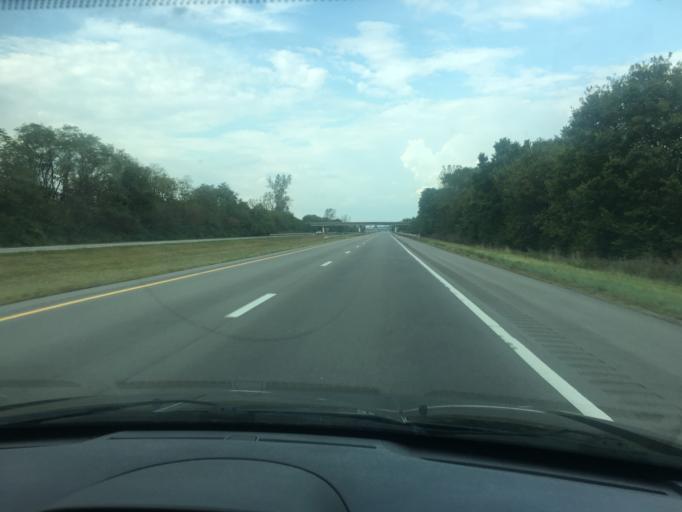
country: US
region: Ohio
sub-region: Clark County
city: Northridge
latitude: 39.9717
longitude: -83.8169
